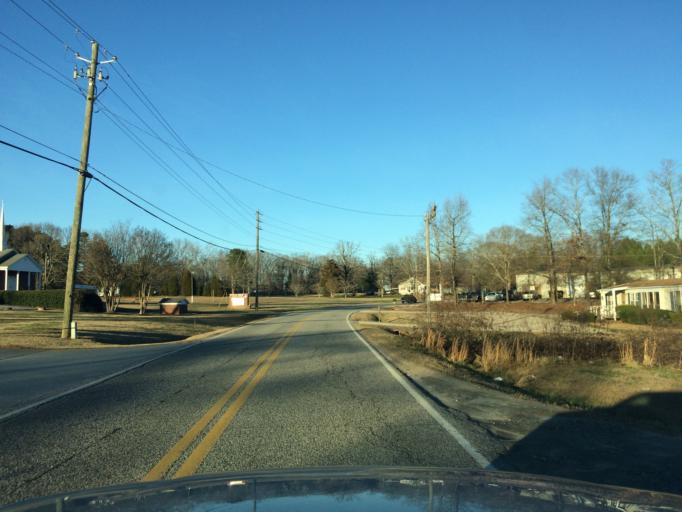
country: US
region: Georgia
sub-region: Barrow County
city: Winder
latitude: 33.9955
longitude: -83.7517
